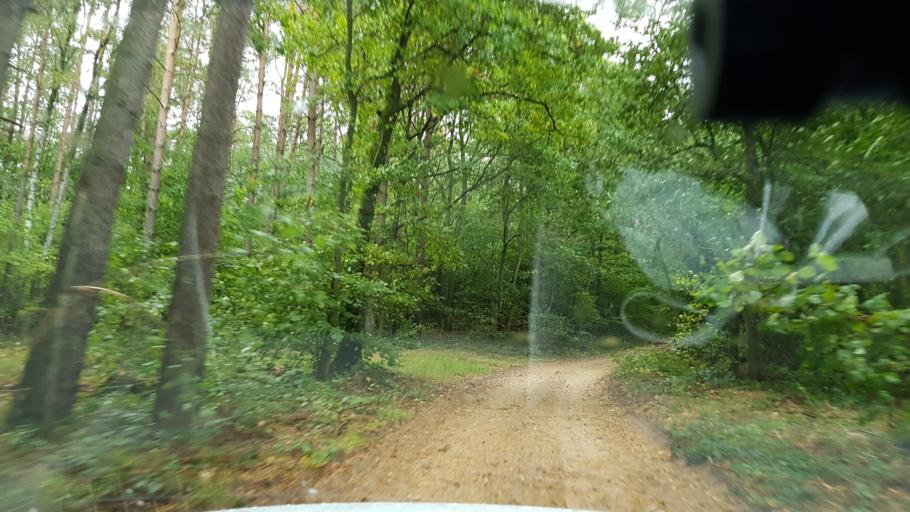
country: PL
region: West Pomeranian Voivodeship
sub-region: Powiat goleniowski
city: Przybiernow
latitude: 53.7481
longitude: 14.7570
